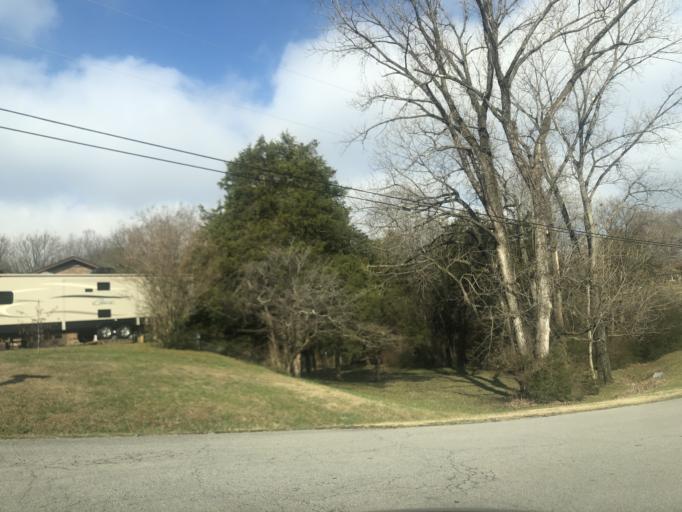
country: US
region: Tennessee
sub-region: Rutherford County
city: La Vergne
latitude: 36.0803
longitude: -86.6562
